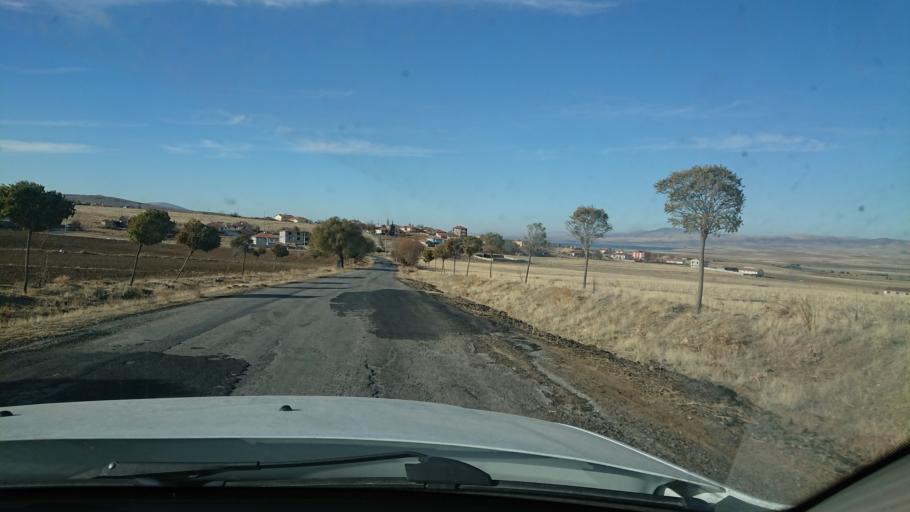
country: TR
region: Aksaray
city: Sariyahsi
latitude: 38.9757
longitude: 33.8573
